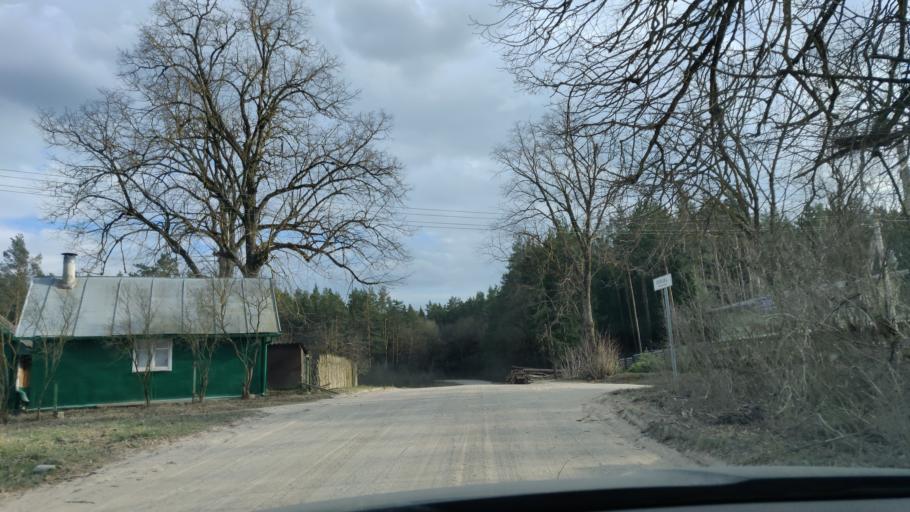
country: LT
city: Lentvaris
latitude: 54.6030
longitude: 25.0754
